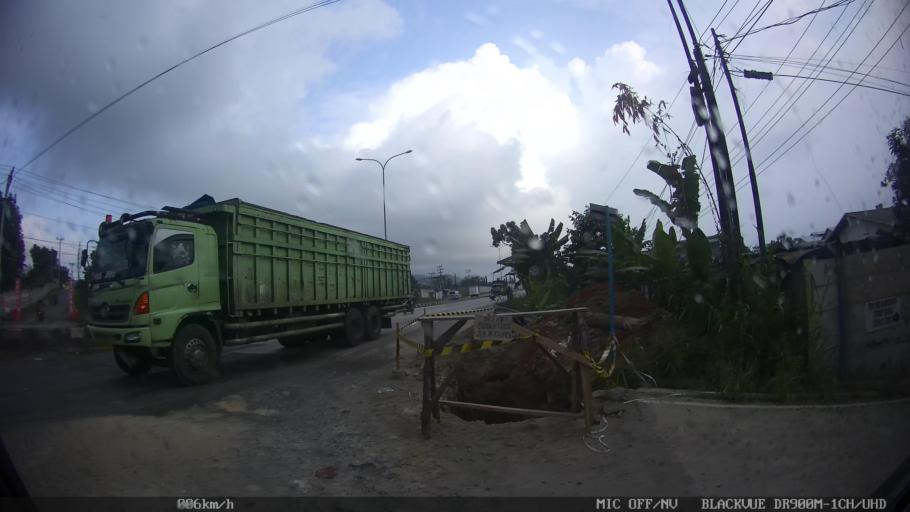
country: ID
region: Lampung
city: Bandarlampung
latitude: -5.4123
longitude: 105.2949
